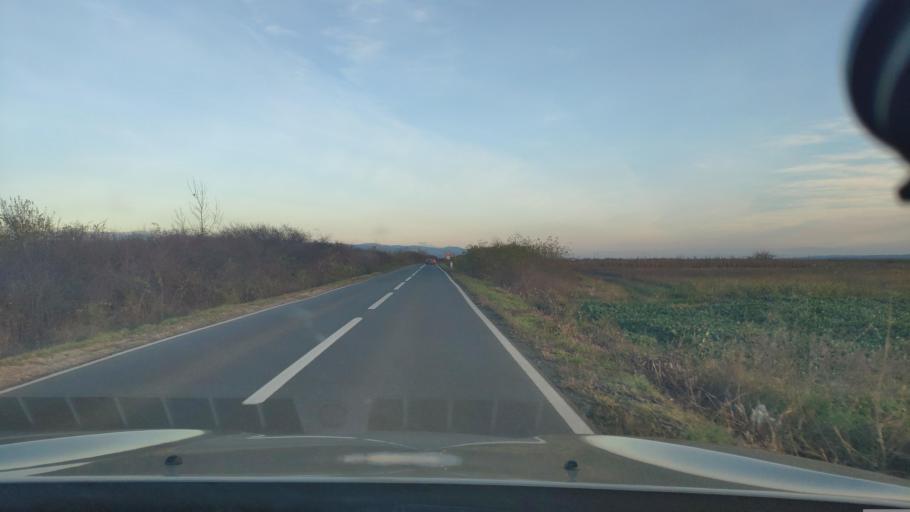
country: RO
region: Satu Mare
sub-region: Comuna Mediesu Aurit
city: Mediesu Aurit
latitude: 47.7683
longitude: 23.1554
